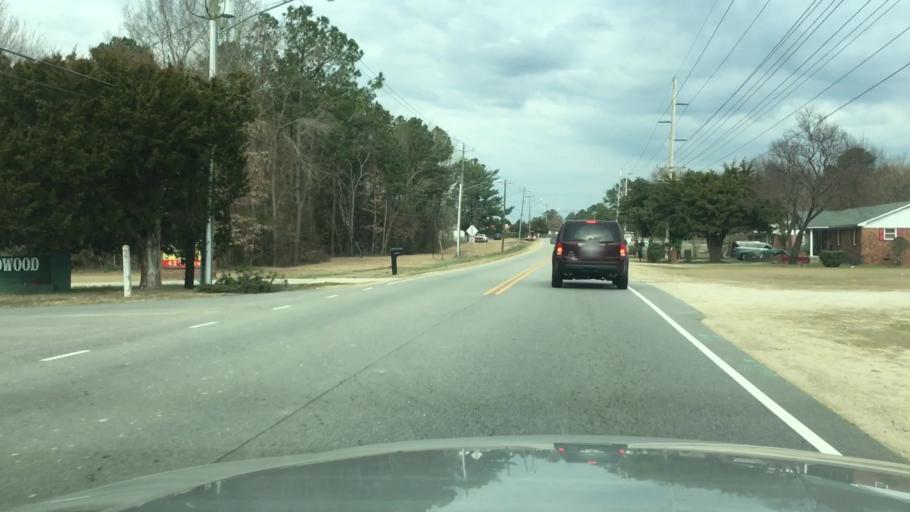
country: US
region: North Carolina
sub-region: Hoke County
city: Rockfish
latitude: 35.0217
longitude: -79.0024
